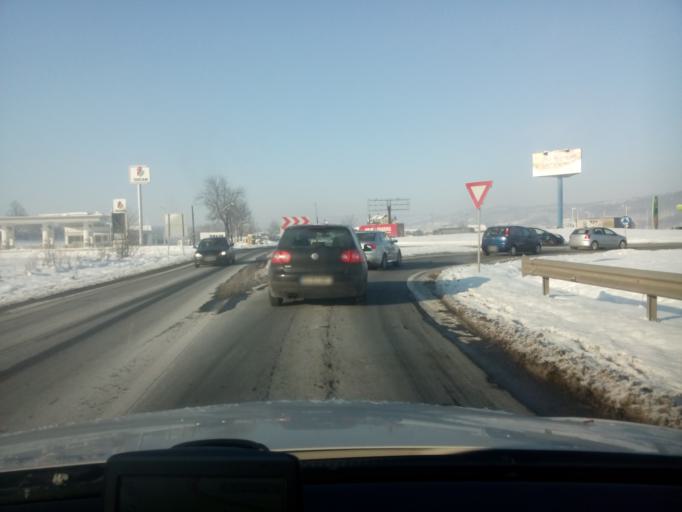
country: RO
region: Sibiu
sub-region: Comuna Selimbar
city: Vestem
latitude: 45.6998
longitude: 24.2487
